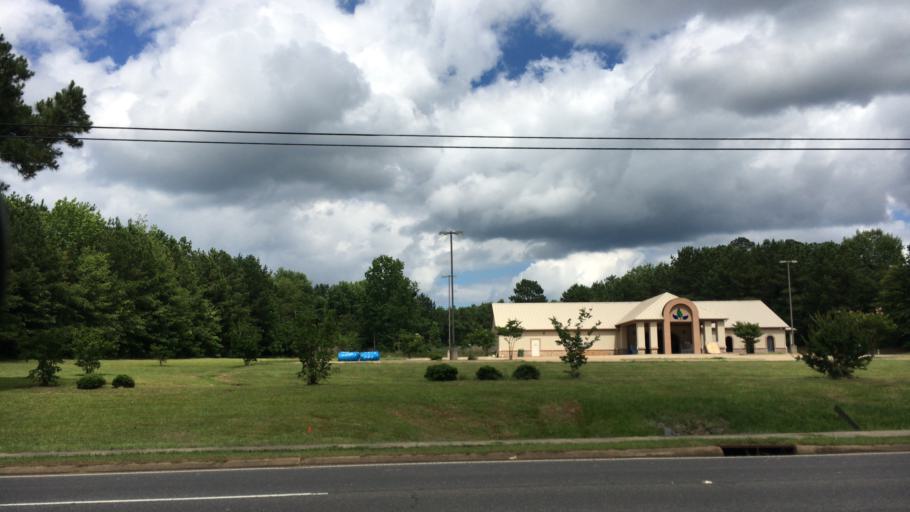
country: US
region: Louisiana
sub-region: Lincoln Parish
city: Ruston
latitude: 32.5009
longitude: -92.6369
